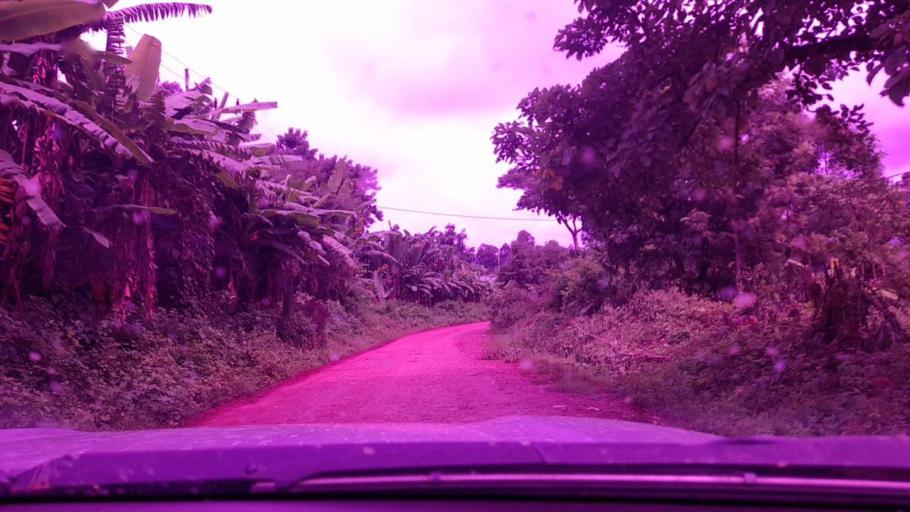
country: ET
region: Southern Nations, Nationalities, and People's Region
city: Bonga
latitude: 7.5449
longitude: 35.8759
